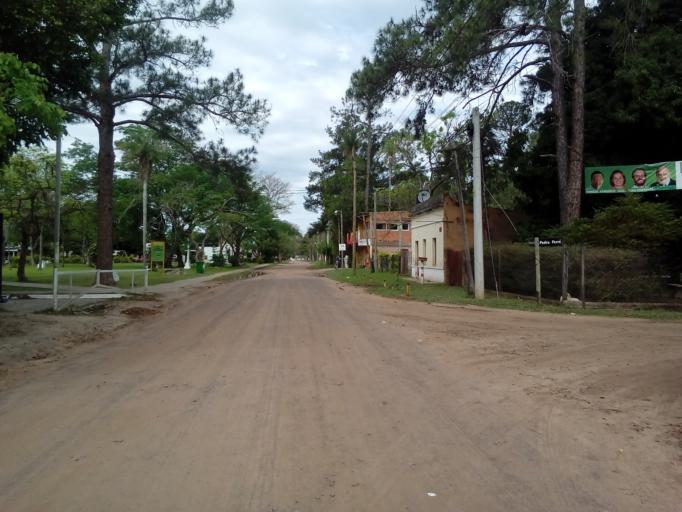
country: AR
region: Corrientes
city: San Luis del Palmar
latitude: -27.4573
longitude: -58.6599
